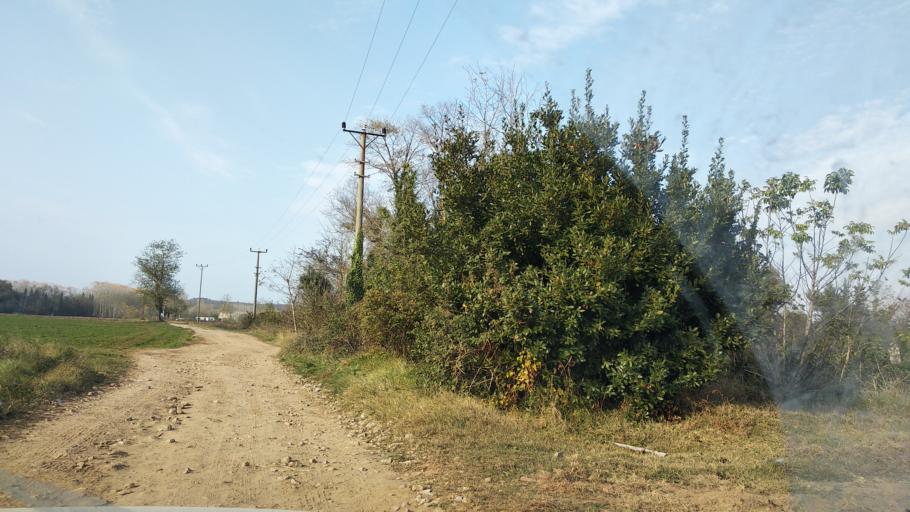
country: TR
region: Sakarya
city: Karasu
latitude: 41.0886
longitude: 30.5972
